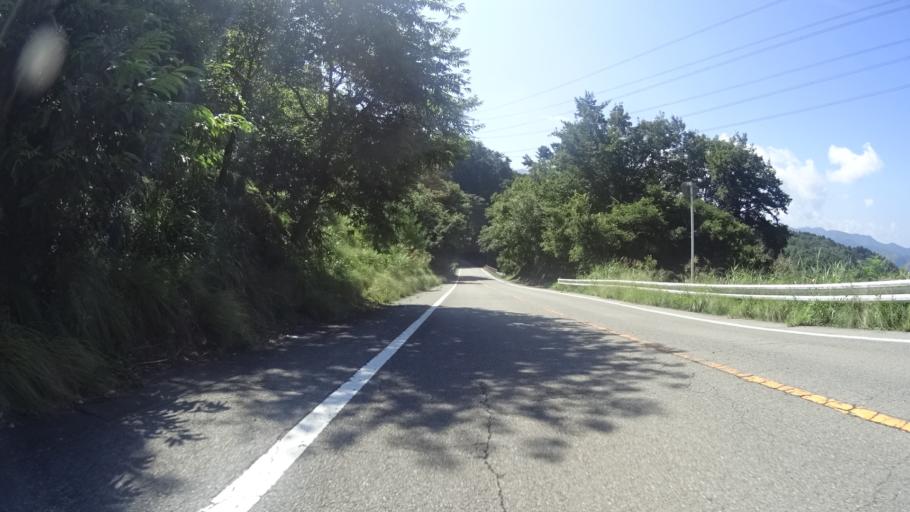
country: JP
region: Yamanashi
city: Enzan
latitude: 35.7455
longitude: 138.8085
